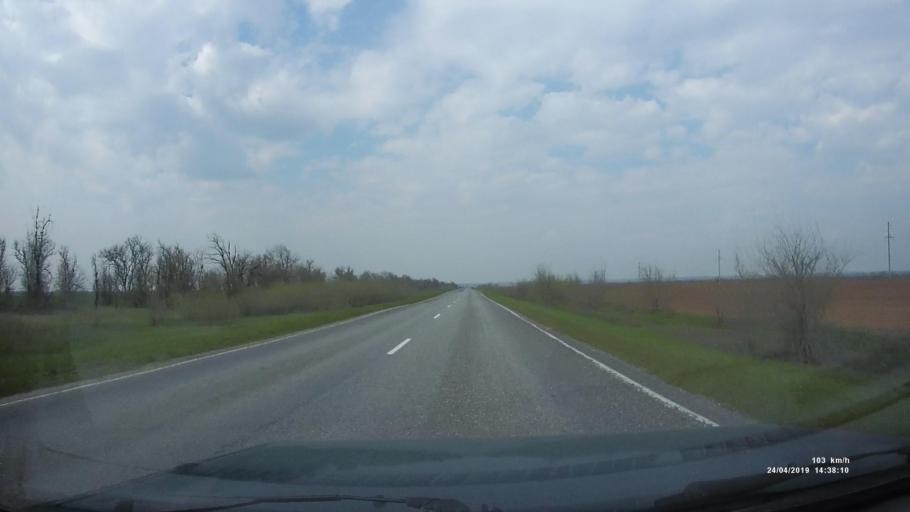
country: RU
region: Rostov
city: Remontnoye
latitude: 46.3972
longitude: 43.8861
